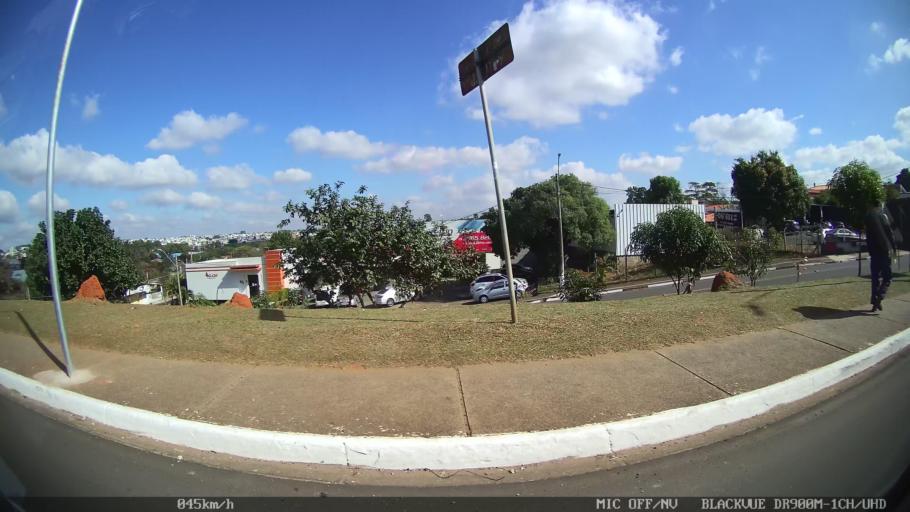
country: BR
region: Sao Paulo
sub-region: Hortolandia
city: Hortolandia
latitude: -22.8591
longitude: -47.2163
